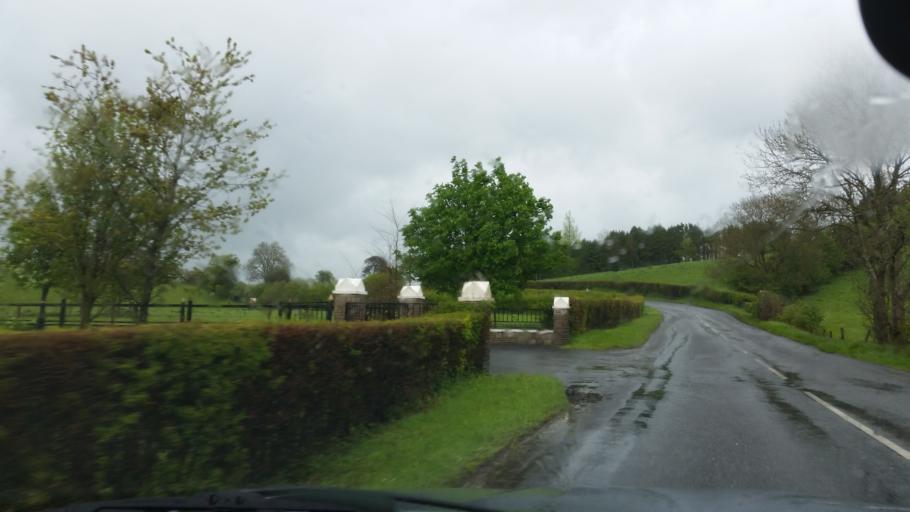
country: GB
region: Northern Ireland
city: Fintona
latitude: 54.5166
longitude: -7.2988
